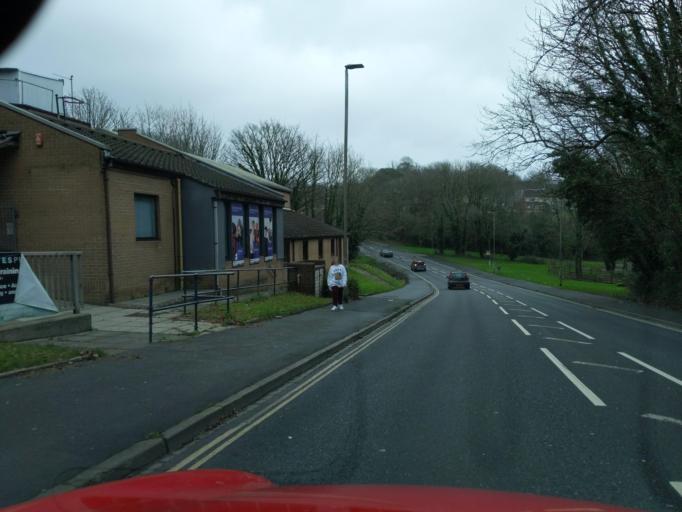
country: GB
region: England
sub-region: Plymouth
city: Plymouth
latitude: 50.4024
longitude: -4.1543
